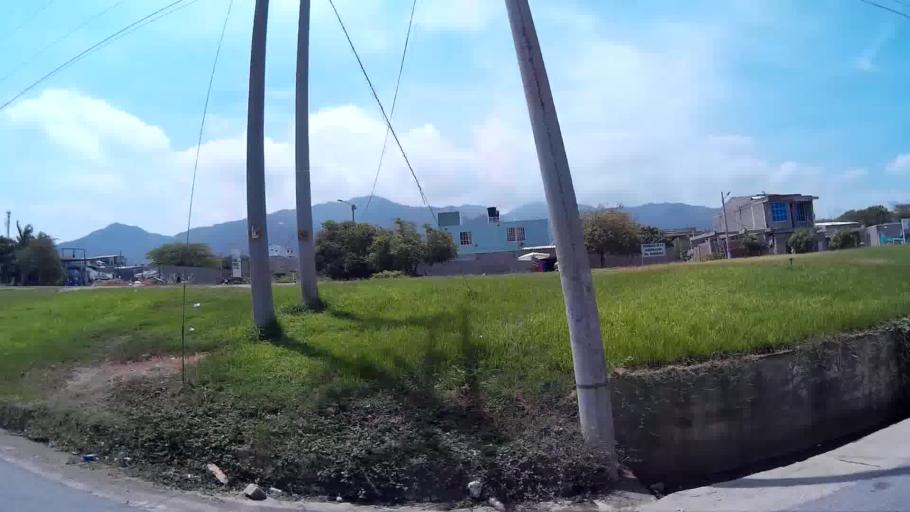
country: CO
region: Magdalena
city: Santa Marta
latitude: 11.1420
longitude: -74.2243
